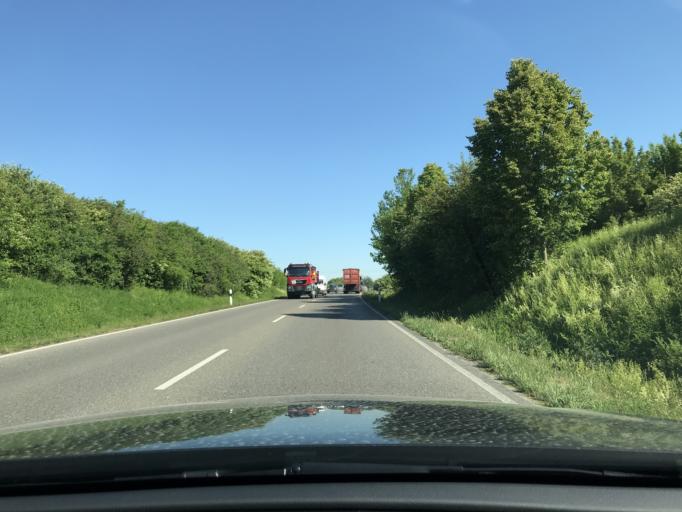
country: DE
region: Baden-Wuerttemberg
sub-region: Regierungsbezirk Stuttgart
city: Fellbach
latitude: 48.8220
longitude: 9.2909
